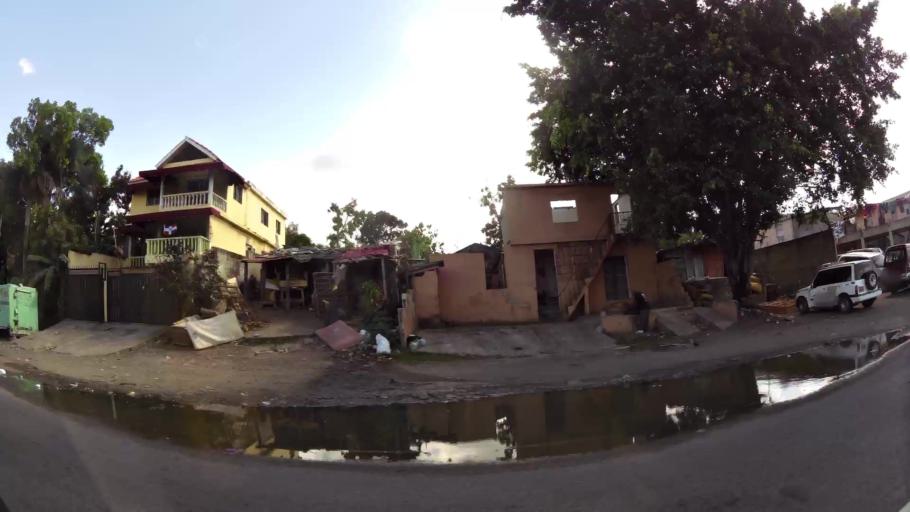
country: DO
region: Santo Domingo
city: Santo Domingo Oeste
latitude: 18.5499
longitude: -70.0506
